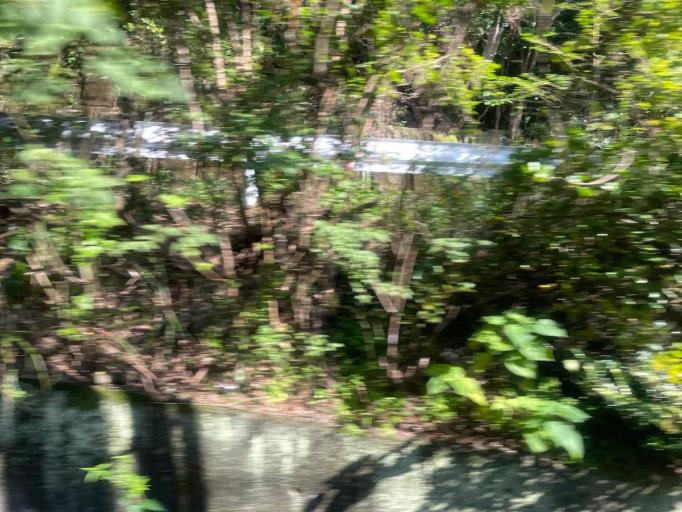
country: JP
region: Mie
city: Toba
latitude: 34.4753
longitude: 136.8045
